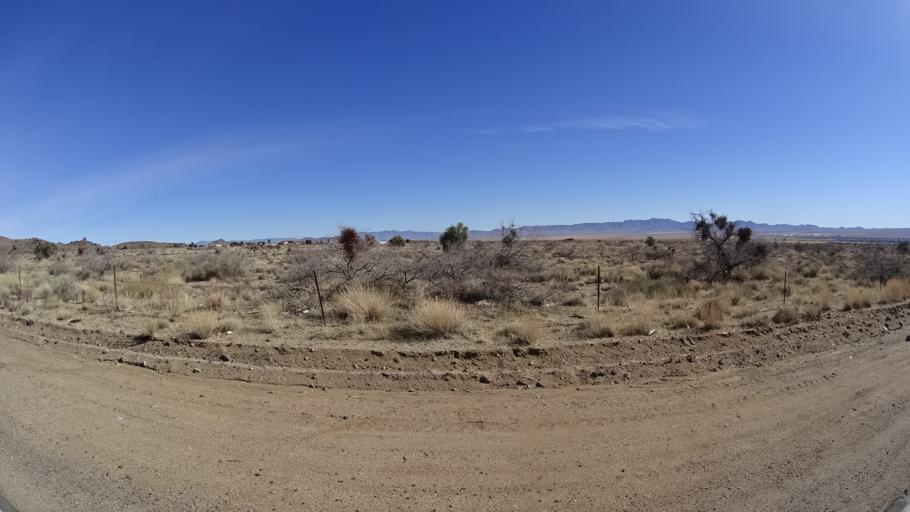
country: US
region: Arizona
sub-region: Mohave County
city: New Kingman-Butler
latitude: 35.2831
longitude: -114.0535
